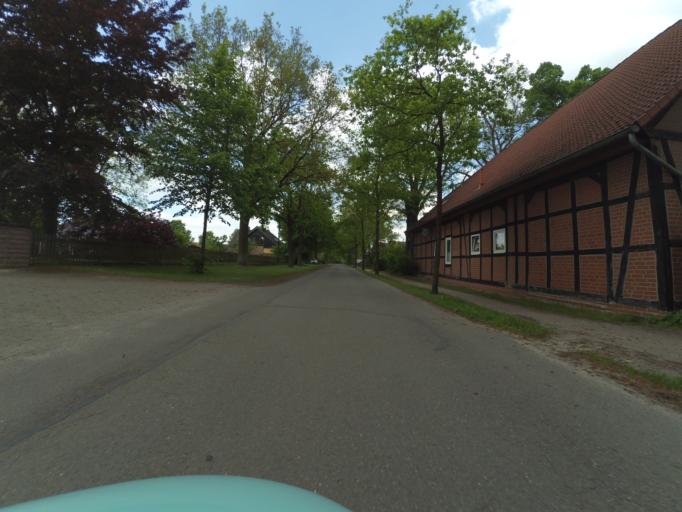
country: DE
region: Lower Saxony
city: Wietze
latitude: 52.5670
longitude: 9.8437
